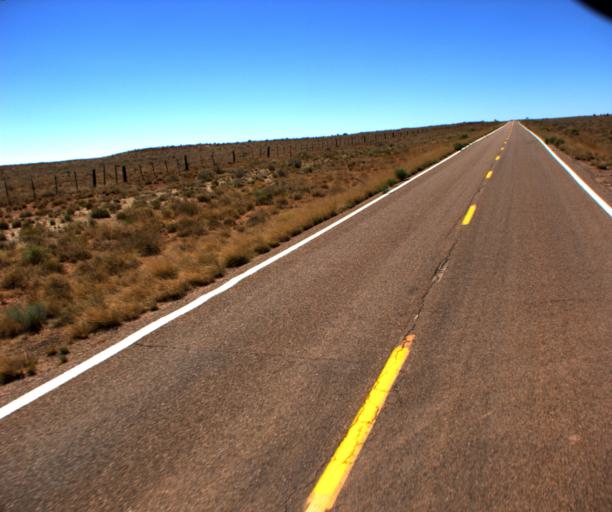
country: US
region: Arizona
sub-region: Navajo County
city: Winslow
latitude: 34.9407
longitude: -110.6435
